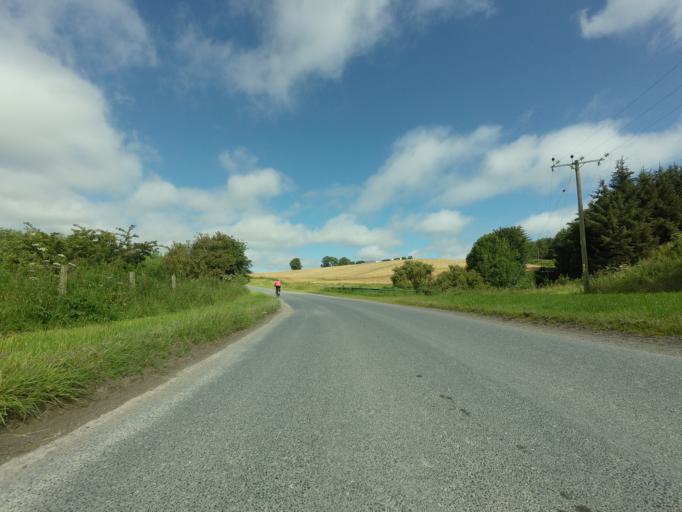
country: GB
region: Scotland
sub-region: Aberdeenshire
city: Turriff
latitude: 57.5654
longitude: -2.4926
